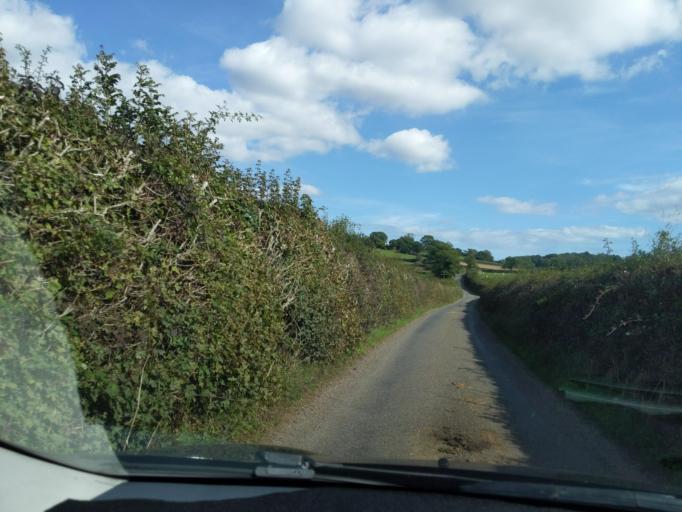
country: GB
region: England
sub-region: Devon
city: Ipplepen
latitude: 50.4618
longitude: -3.6265
